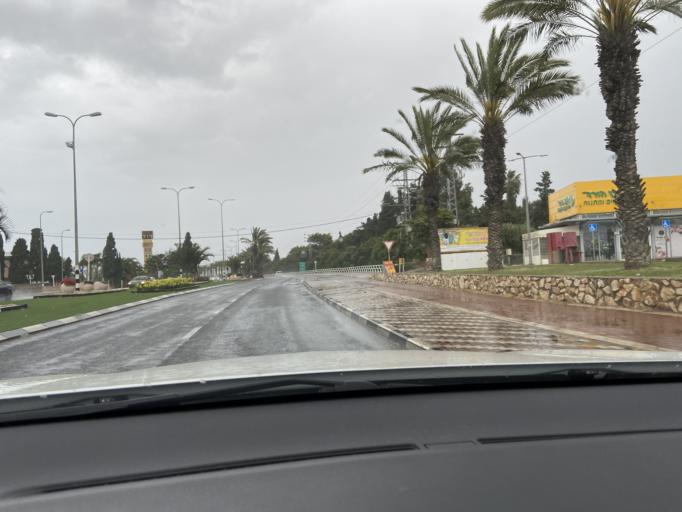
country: IL
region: Northern District
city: El Mazra`a
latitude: 32.9902
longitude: 35.0960
